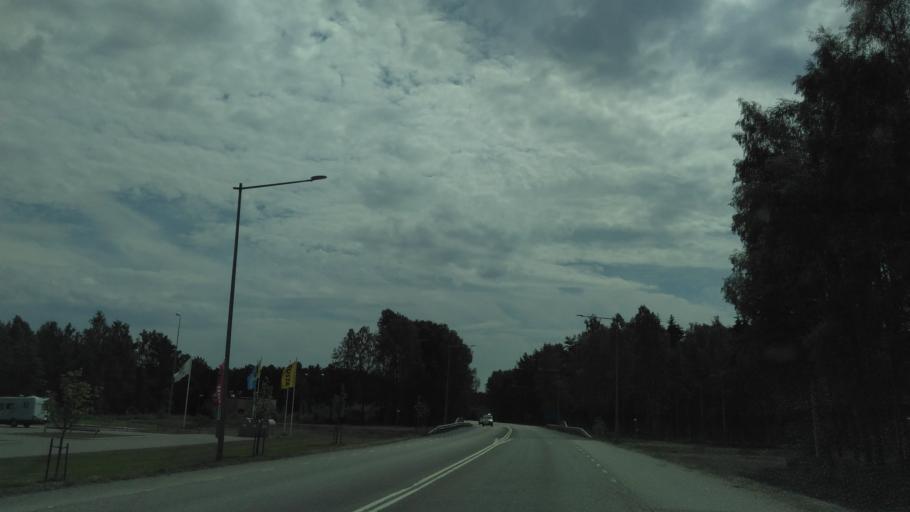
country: SE
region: Vaestra Goetaland
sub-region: Lidkopings Kommun
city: Lidkoping
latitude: 58.4929
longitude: 13.1821
